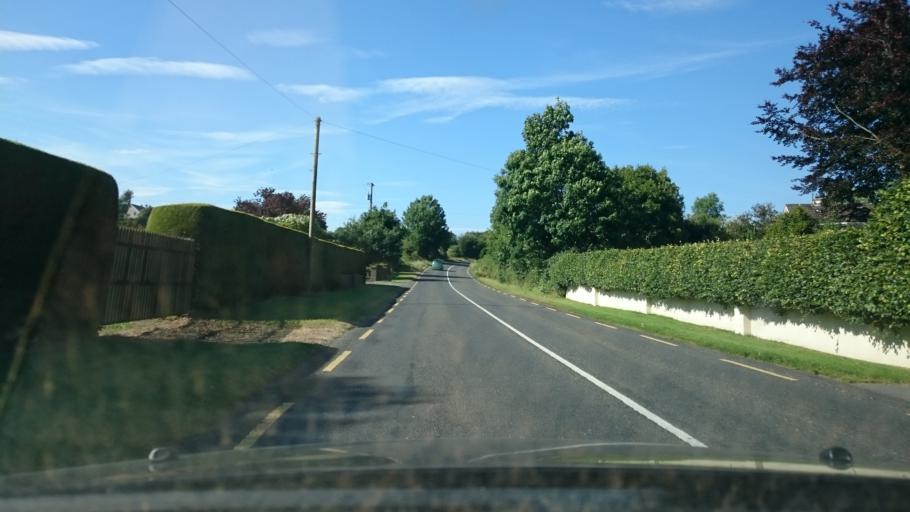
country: IE
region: Leinster
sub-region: Kilkenny
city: Graiguenamanagh
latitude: 52.5489
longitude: -6.9582
